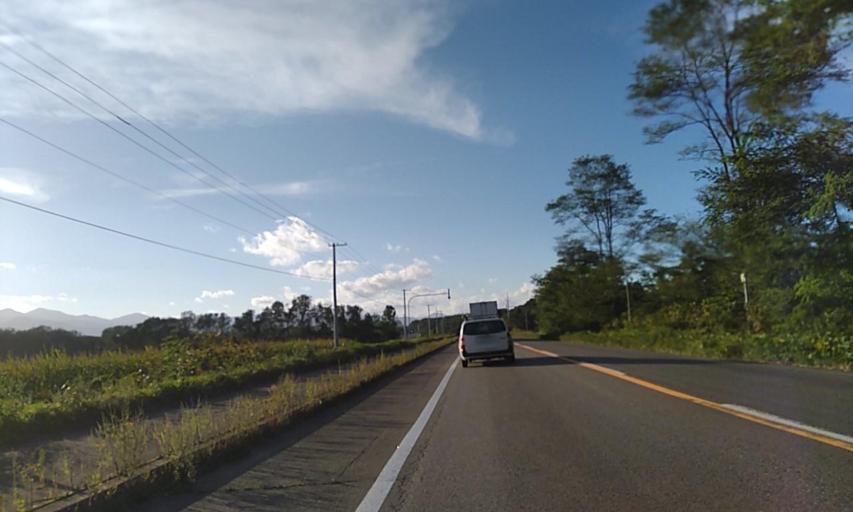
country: JP
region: Hokkaido
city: Obihiro
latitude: 42.9305
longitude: 142.9793
